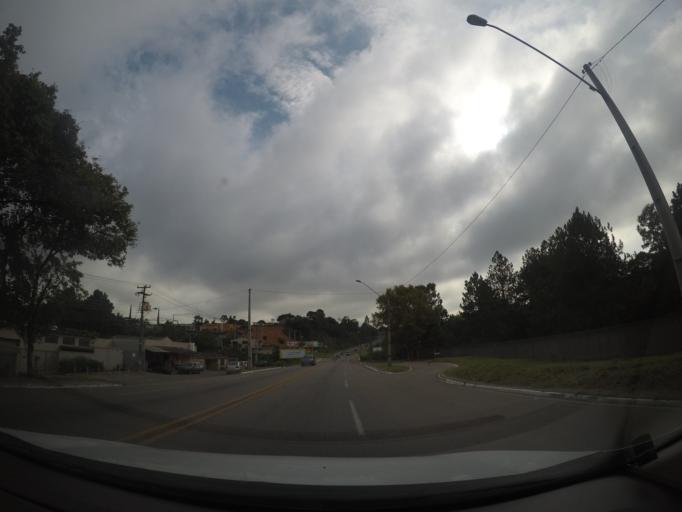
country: BR
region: Parana
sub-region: Colombo
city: Colombo
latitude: -25.3646
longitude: -49.2204
